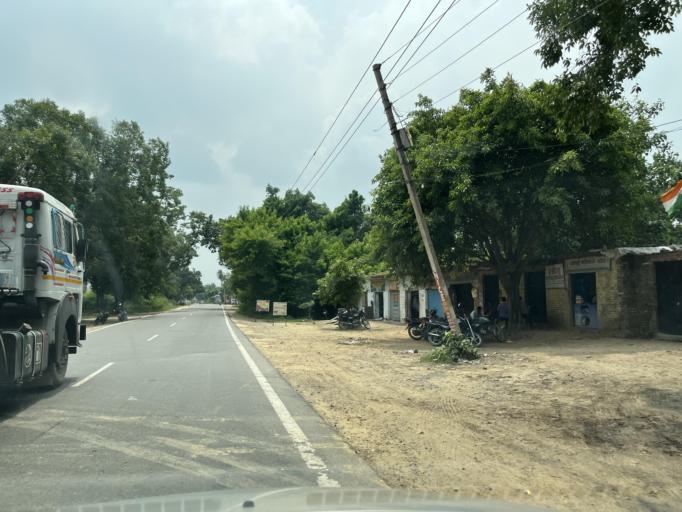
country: IN
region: Uttar Pradesh
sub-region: Bijnor
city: Najibabad
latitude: 29.5815
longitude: 78.3385
